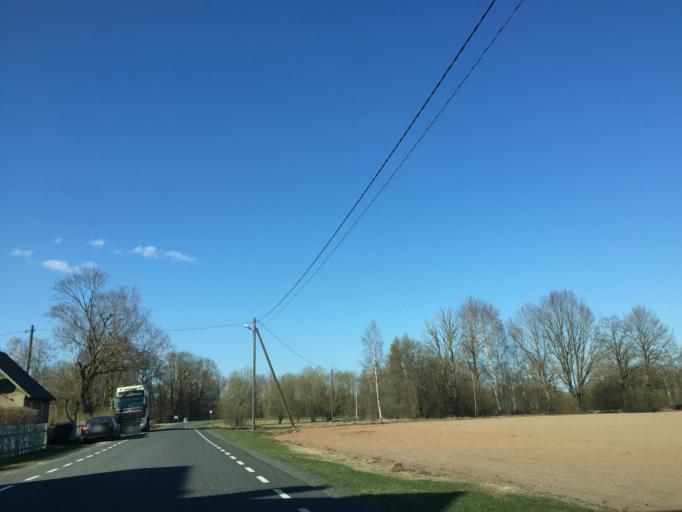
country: EE
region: Valgamaa
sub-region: Torva linn
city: Torva
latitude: 58.2355
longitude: 25.8815
